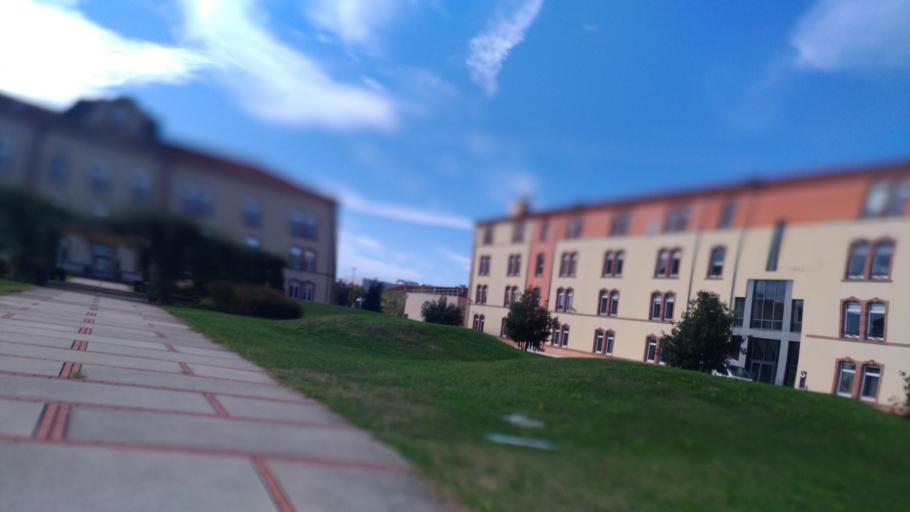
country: FR
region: Midi-Pyrenees
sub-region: Departement du Tarn
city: Albi
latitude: 43.9193
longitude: 2.1384
